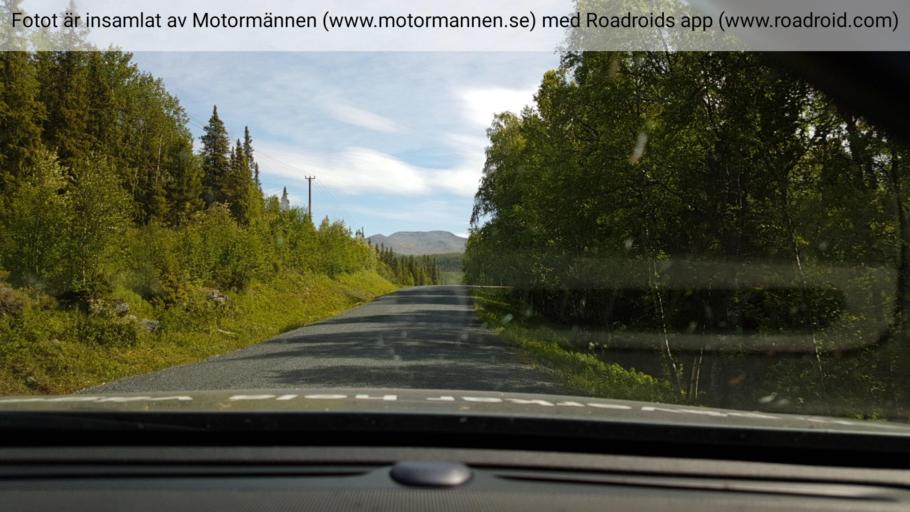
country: SE
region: Vaesterbotten
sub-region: Vilhelmina Kommun
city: Sjoberg
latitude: 65.2754
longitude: 15.3459
